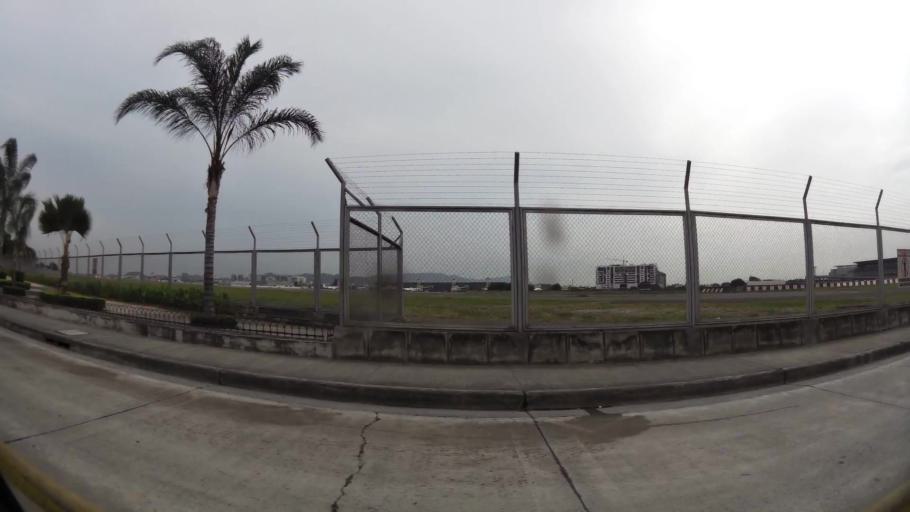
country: EC
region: Guayas
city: Eloy Alfaro
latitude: -2.1469
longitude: -79.8767
